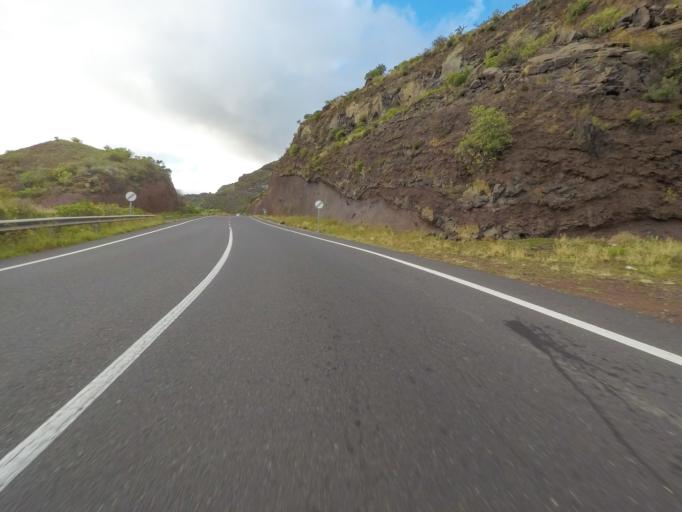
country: ES
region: Canary Islands
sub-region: Provincia de Santa Cruz de Tenerife
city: San Sebastian de la Gomera
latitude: 28.1197
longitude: -17.1434
